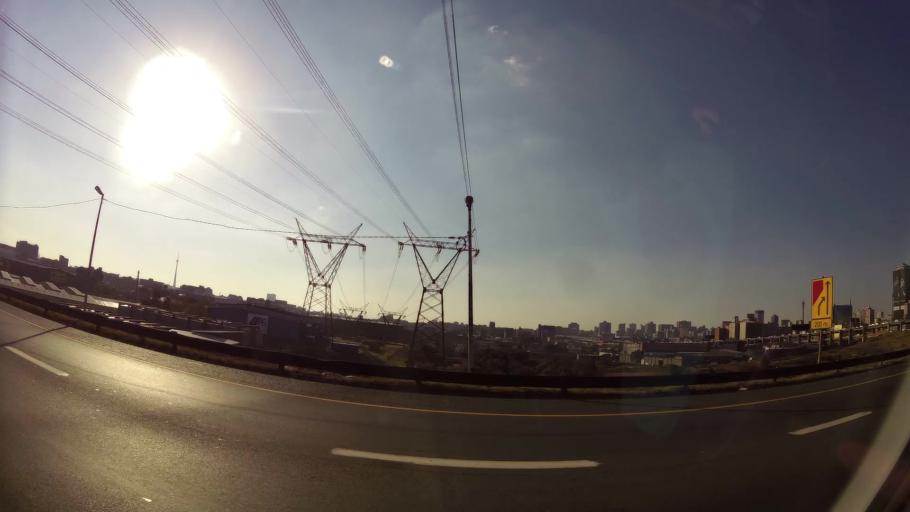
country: ZA
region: Gauteng
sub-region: City of Johannesburg Metropolitan Municipality
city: Johannesburg
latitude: -26.2111
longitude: 28.0289
